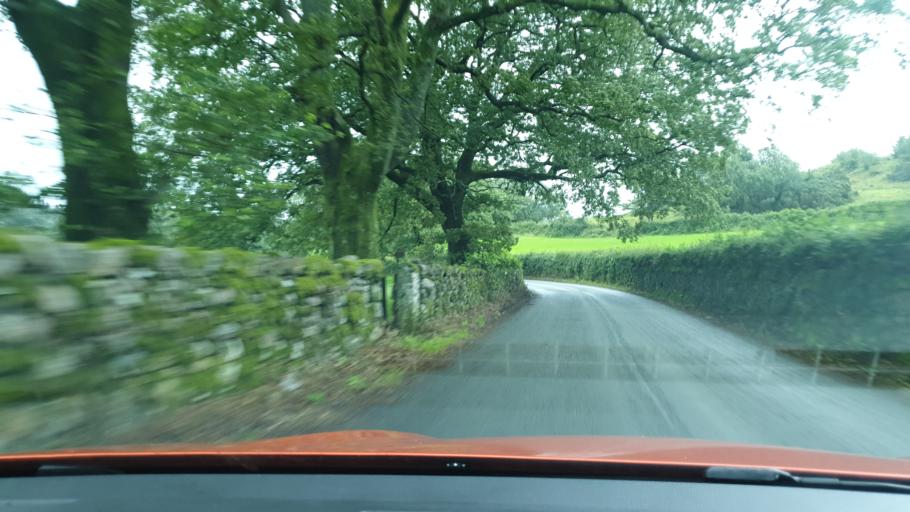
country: GB
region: England
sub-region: Cumbria
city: Seascale
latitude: 54.3979
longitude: -3.3479
